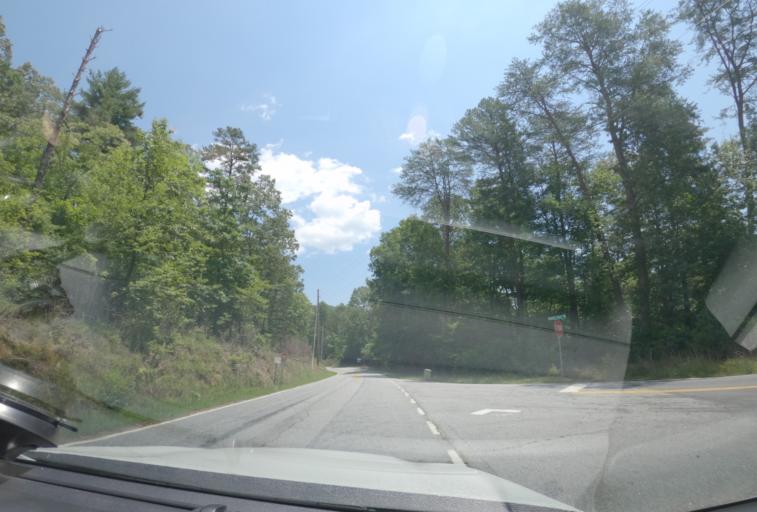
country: US
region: South Carolina
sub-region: Pickens County
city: Pickens
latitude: 34.9689
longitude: -82.8622
